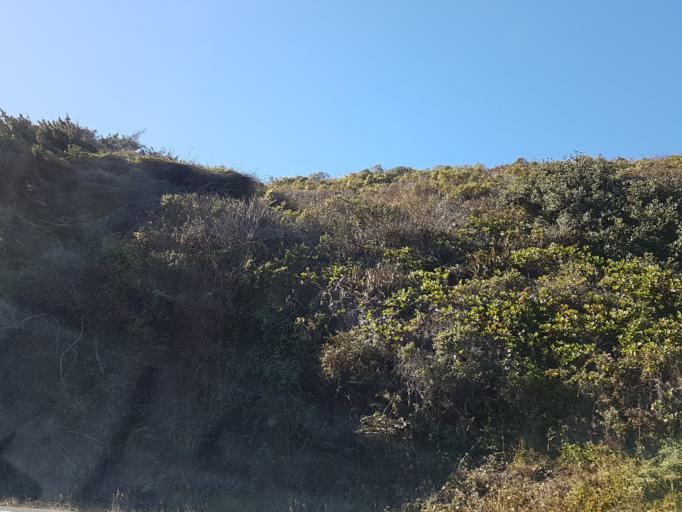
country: US
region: California
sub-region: Mendocino County
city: Boonville
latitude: 39.1009
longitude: -123.7060
